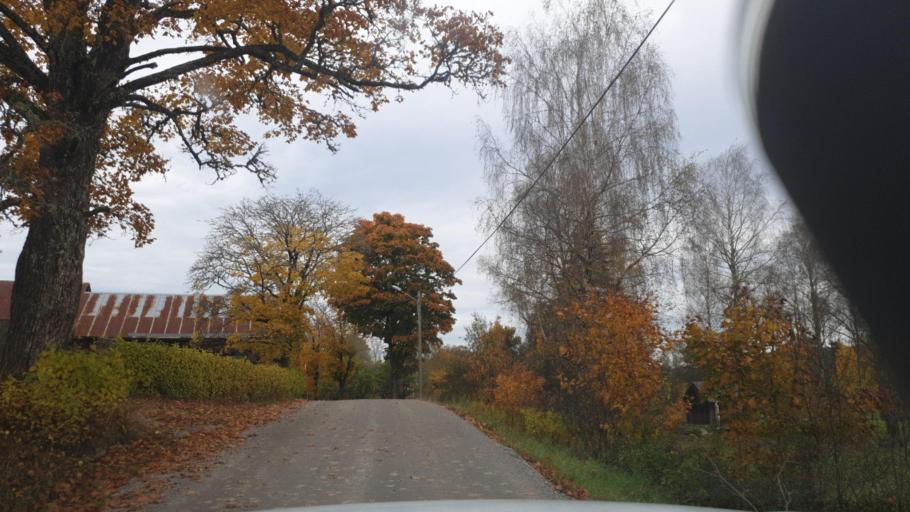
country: SE
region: Vaermland
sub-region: Arvika Kommun
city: Arvika
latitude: 59.6708
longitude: 12.7691
